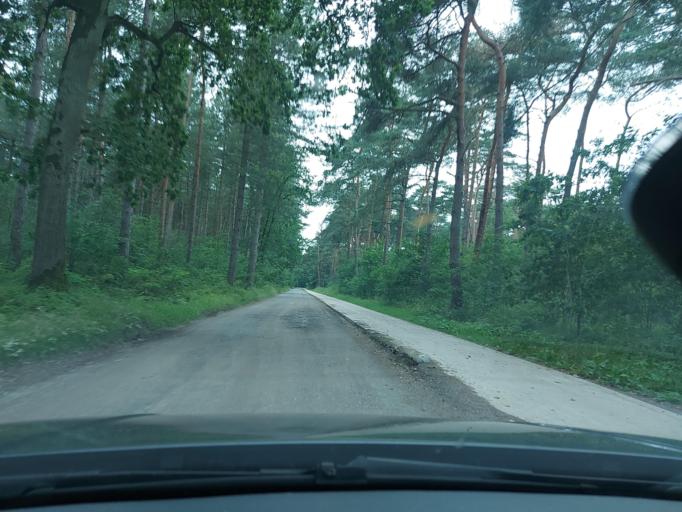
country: BE
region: Flanders
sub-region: Provincie Antwerpen
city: Balen
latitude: 51.1741
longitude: 5.2220
